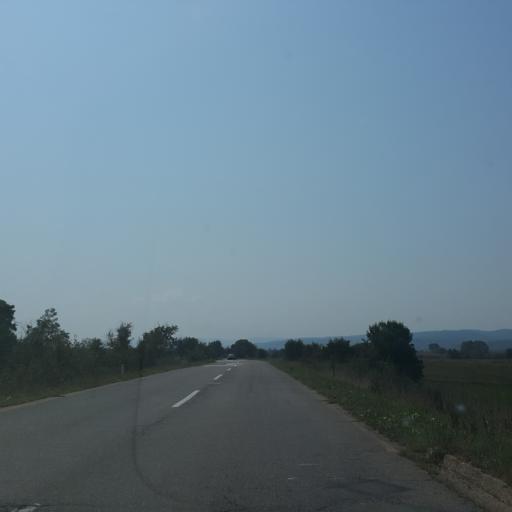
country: RS
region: Central Serbia
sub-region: Zajecarski Okrug
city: Knjazevac
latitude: 43.7049
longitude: 22.3029
